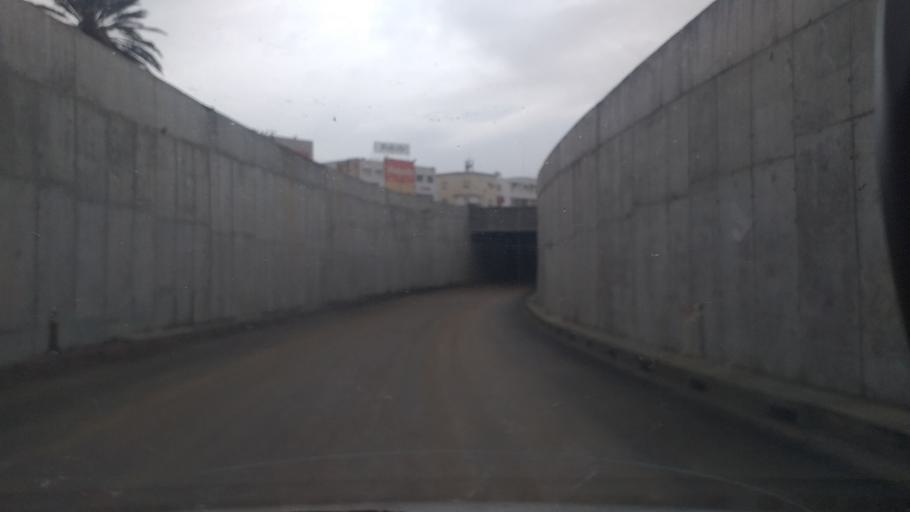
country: TN
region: Ariana
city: Ariana
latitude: 36.8684
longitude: 10.2277
